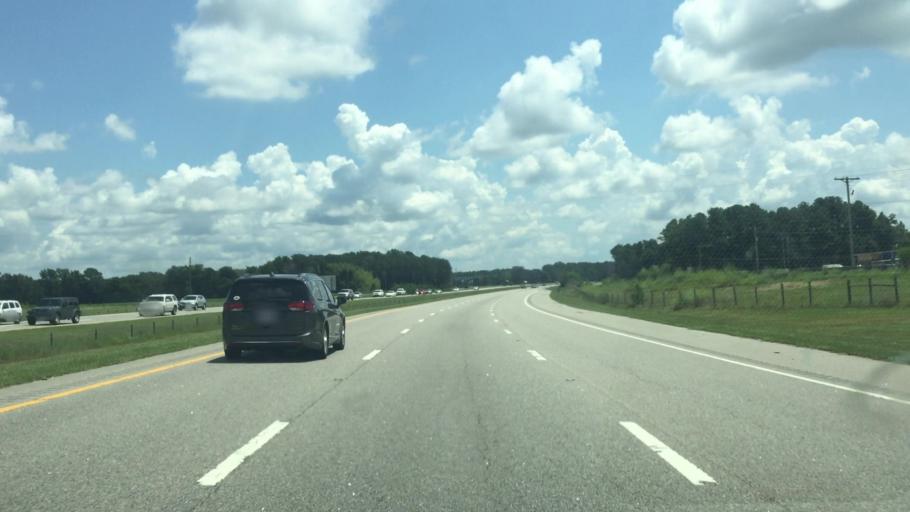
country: US
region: North Carolina
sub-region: Robeson County
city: Lumberton
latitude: 34.5936
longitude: -79.0834
